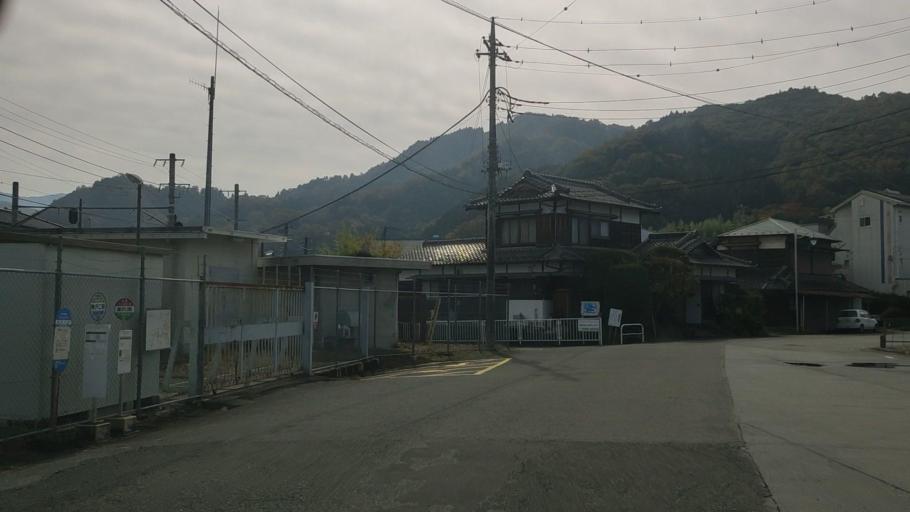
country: JP
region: Yamanashi
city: Ryuo
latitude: 35.5410
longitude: 138.4705
